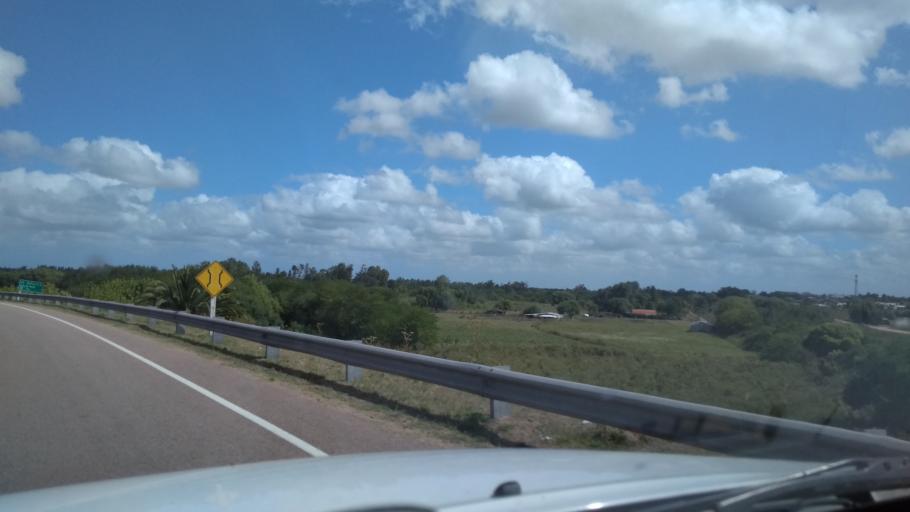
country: UY
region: Canelones
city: Sauce
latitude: -34.6399
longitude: -56.0526
